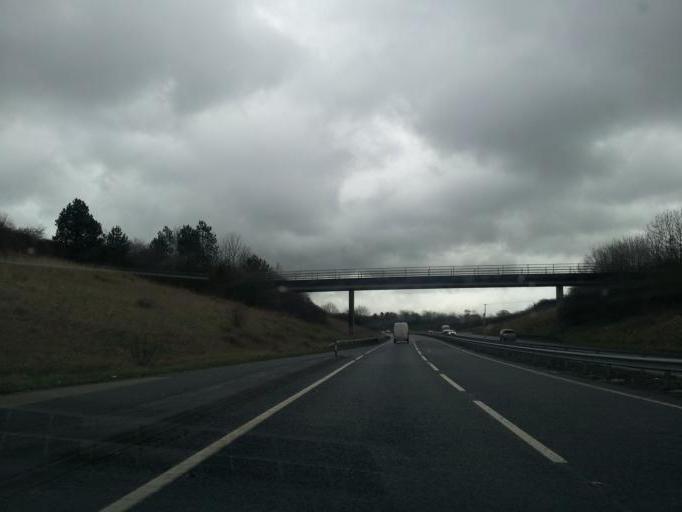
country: GB
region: England
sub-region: Wiltshire
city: Kilmington
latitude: 51.0689
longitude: -2.3389
